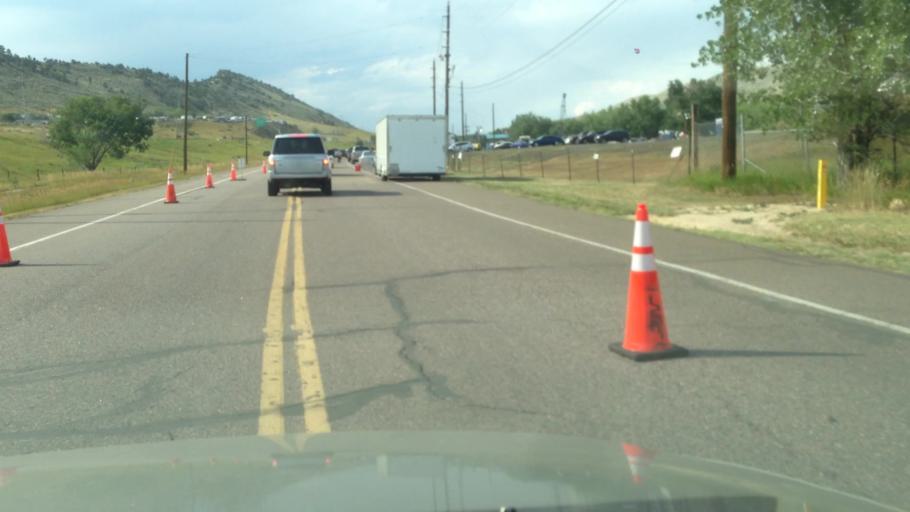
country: US
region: Colorado
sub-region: Jefferson County
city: West Pleasant View
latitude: 39.6635
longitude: -105.1848
